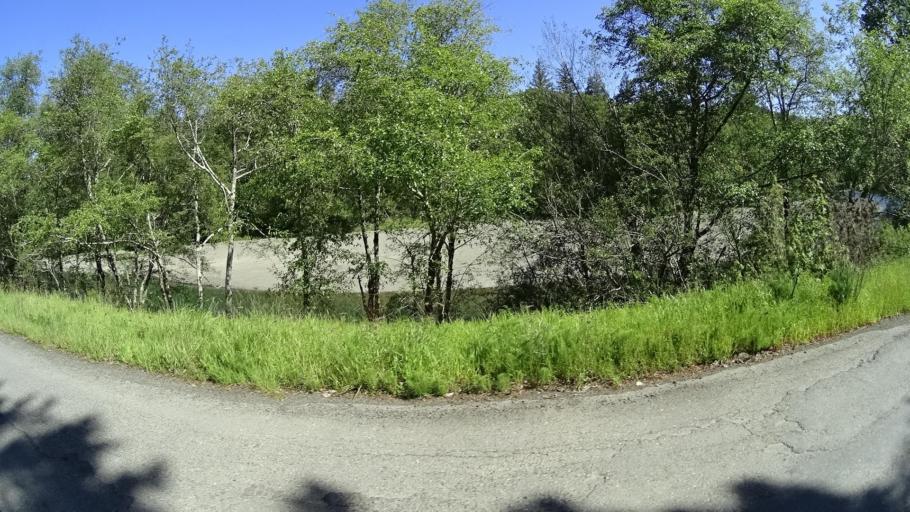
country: US
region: California
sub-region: Humboldt County
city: Rio Dell
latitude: 40.2297
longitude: -124.1451
